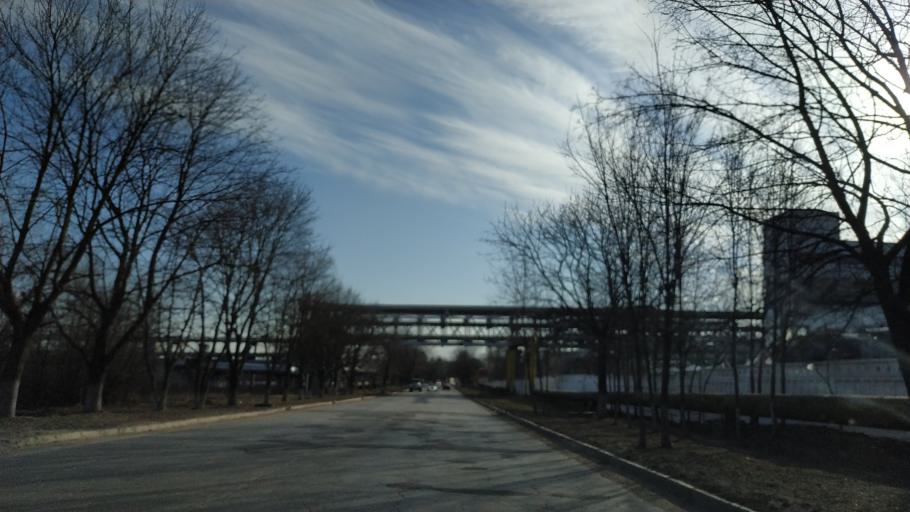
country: MD
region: Chisinau
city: Chisinau
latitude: 47.0294
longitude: 28.8963
